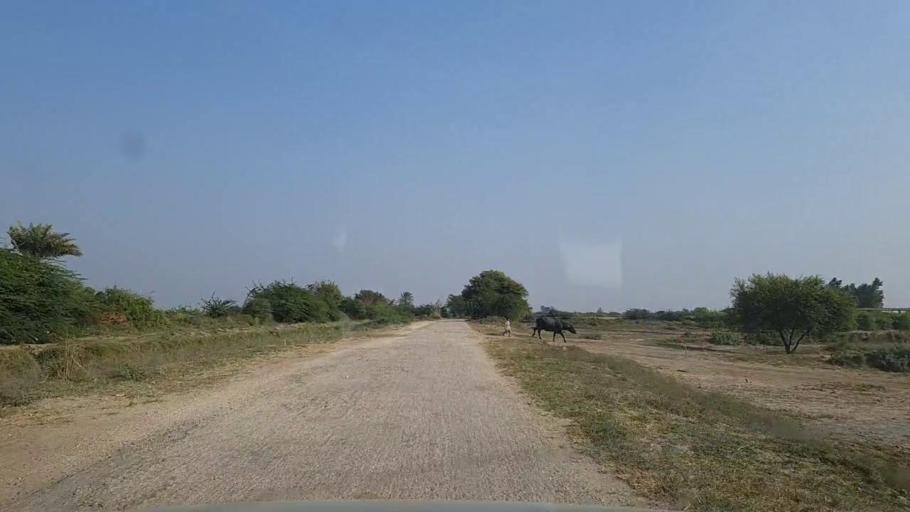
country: PK
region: Sindh
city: Mirpur Sakro
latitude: 24.5958
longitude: 67.5982
